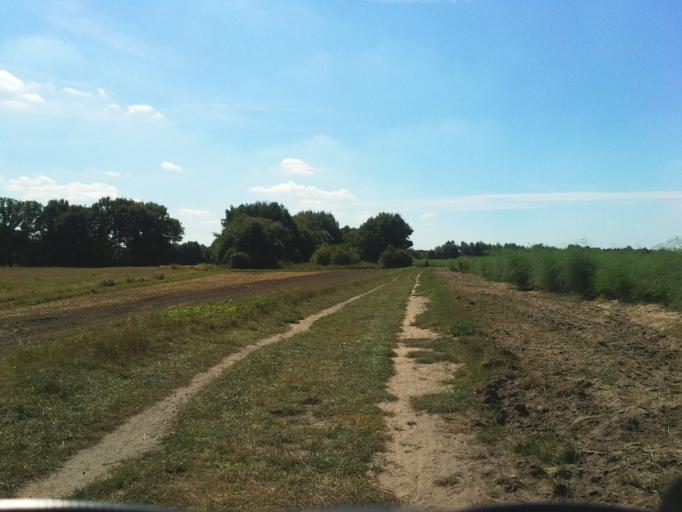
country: DE
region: Lower Saxony
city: Nienburg
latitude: 52.6538
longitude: 9.2390
